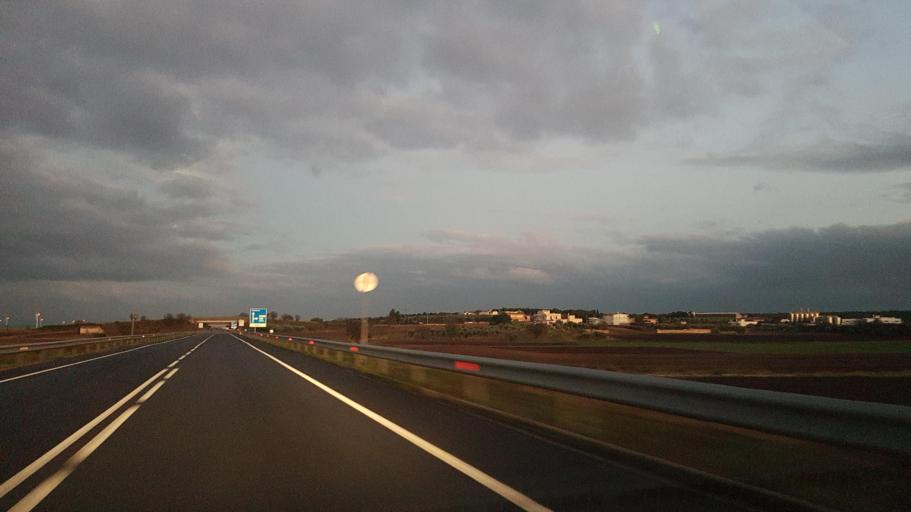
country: IT
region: Apulia
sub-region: Provincia di Taranto
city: Laterza
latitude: 40.6497
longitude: 16.8139
